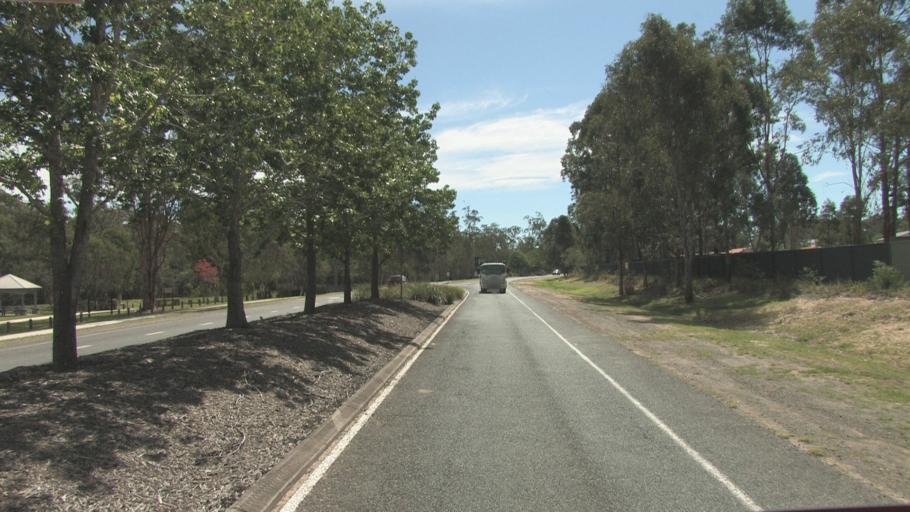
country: AU
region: Queensland
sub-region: Logan
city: North Maclean
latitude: -27.8143
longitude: 152.9646
